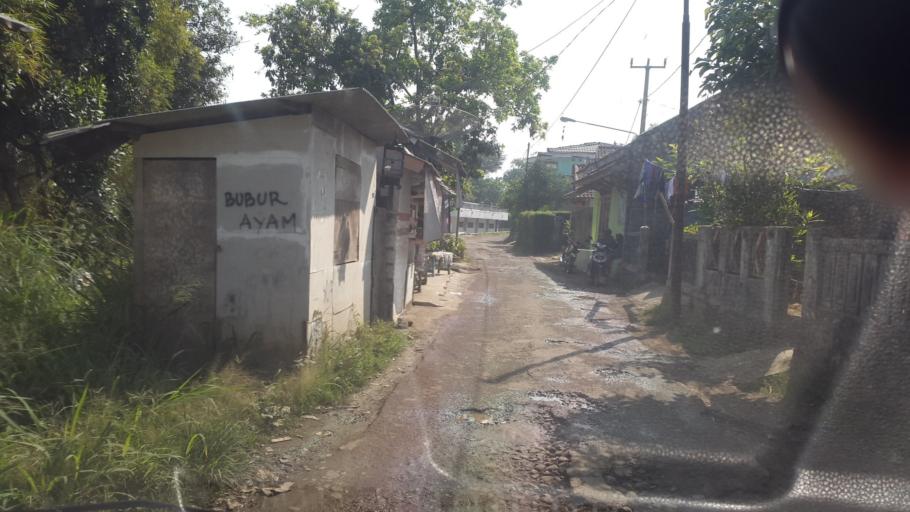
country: ID
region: West Java
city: Sukabumi
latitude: -6.8944
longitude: 106.9033
